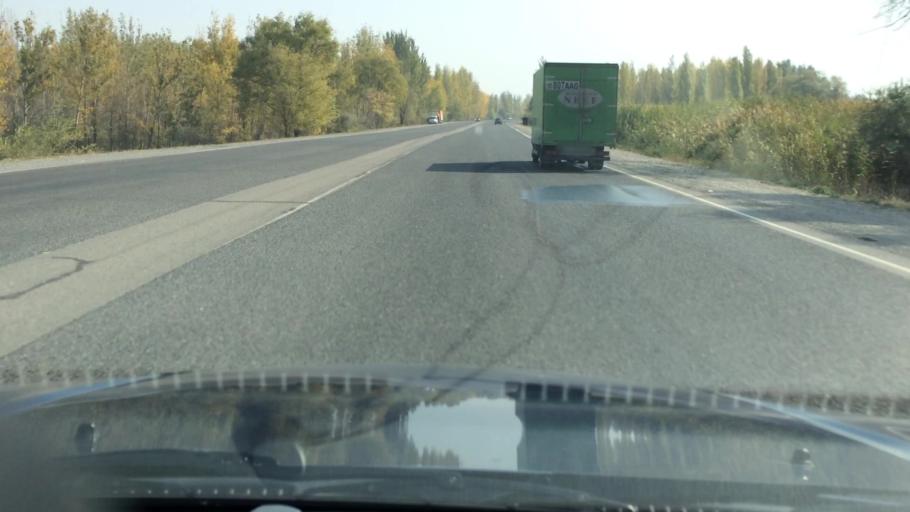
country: KG
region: Chuy
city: Ivanovka
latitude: 42.9390
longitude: 74.9801
